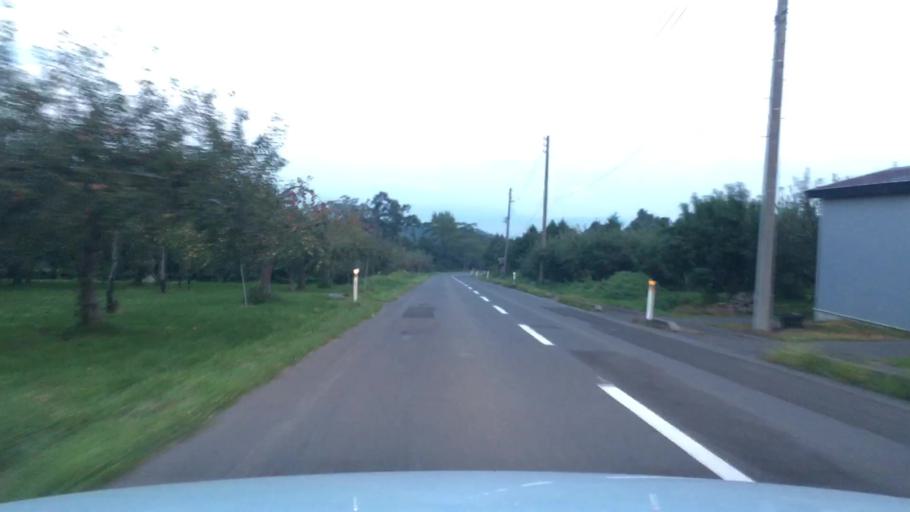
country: JP
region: Aomori
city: Hirosaki
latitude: 40.6774
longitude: 140.3782
